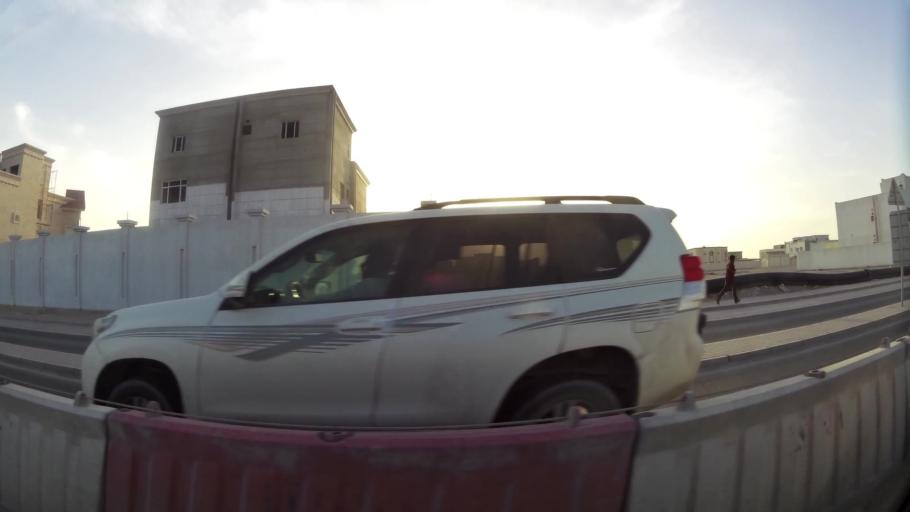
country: QA
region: Al Wakrah
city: Al Wakrah
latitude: 25.1542
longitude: 51.5930
